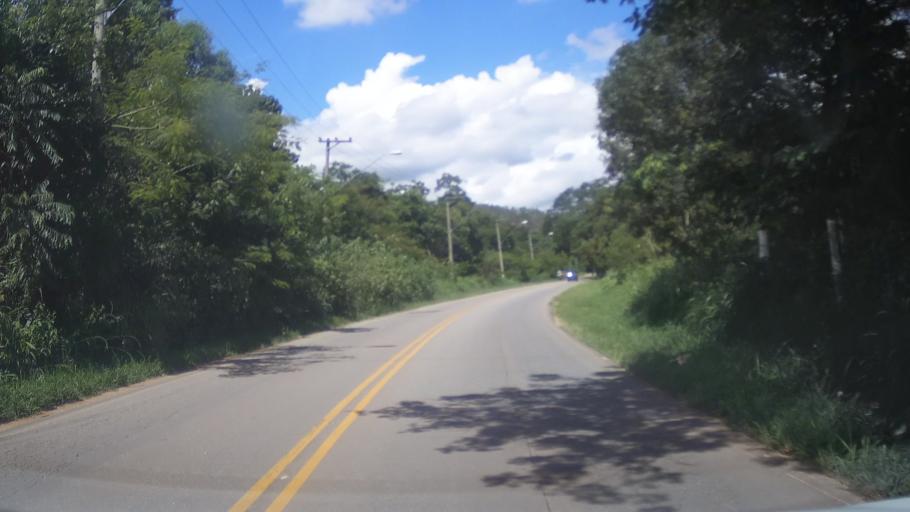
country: BR
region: Sao Paulo
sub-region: Campo Limpo Paulista
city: Campo Limpo Paulista
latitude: -23.2104
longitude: -46.7490
